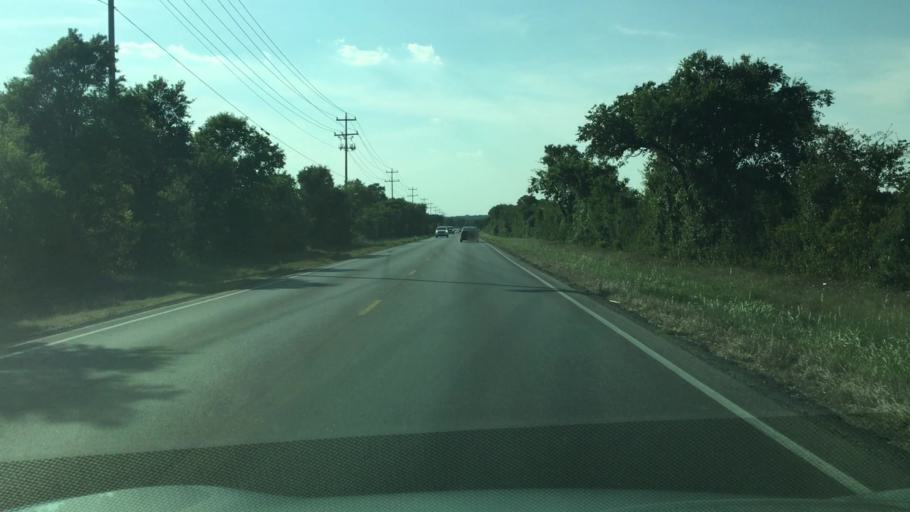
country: US
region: Texas
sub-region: Travis County
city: Shady Hollow
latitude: 30.1087
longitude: -97.9455
